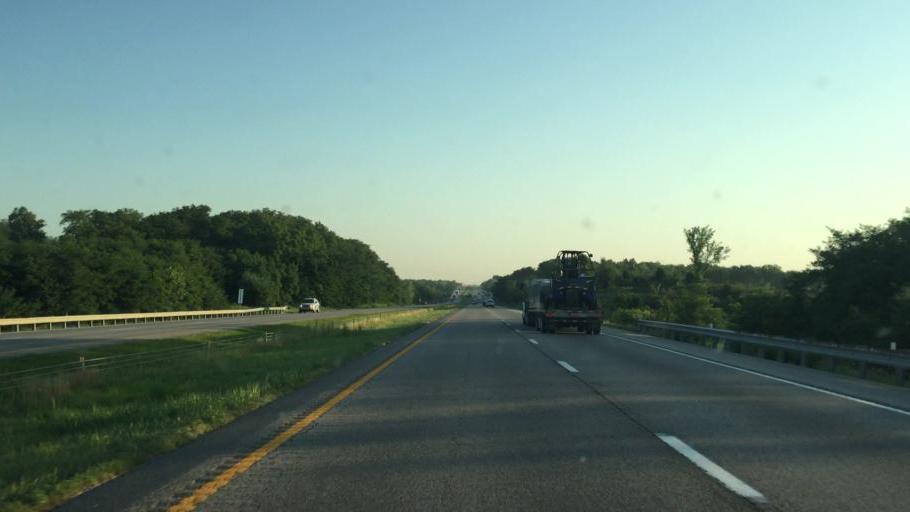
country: US
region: Missouri
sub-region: Platte County
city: Weston
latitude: 39.5632
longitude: -94.7881
